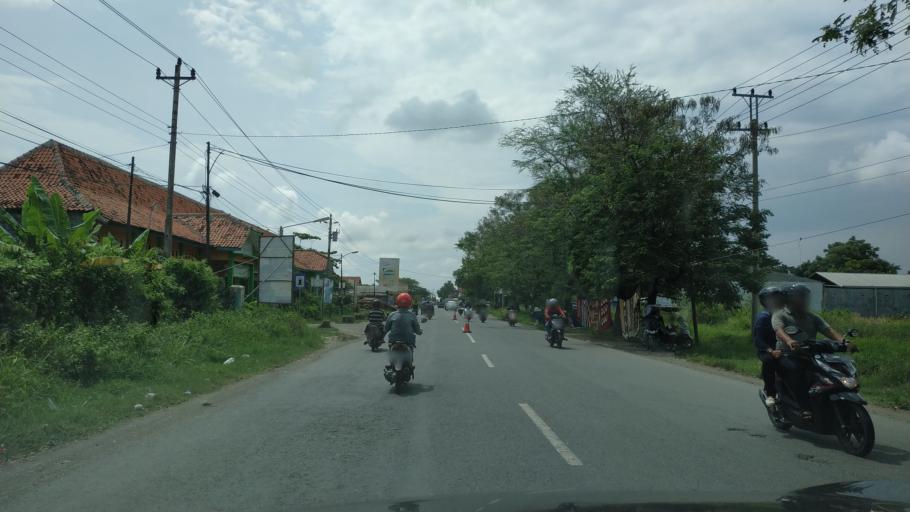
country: ID
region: Central Java
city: Adiwerna
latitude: -6.9331
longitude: 109.1251
